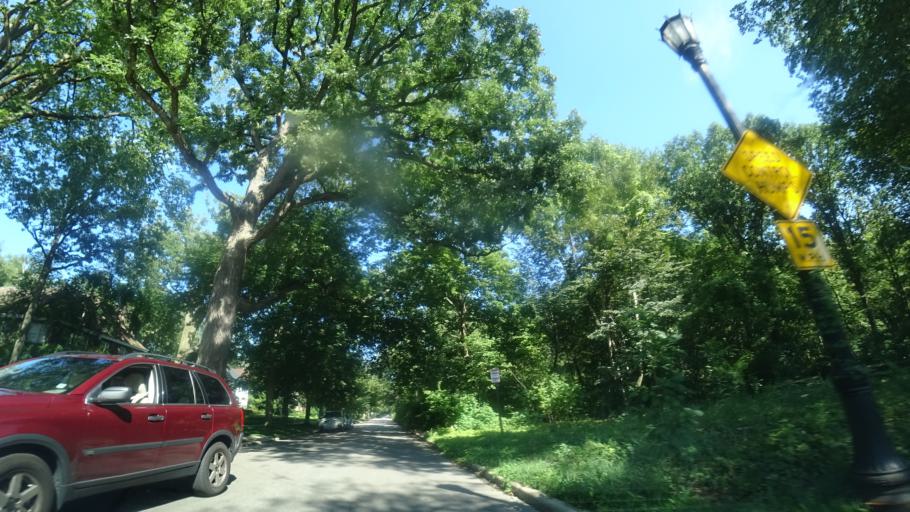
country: US
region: Illinois
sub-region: Cook County
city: Wilmette
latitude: 42.0608
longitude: -87.7129
